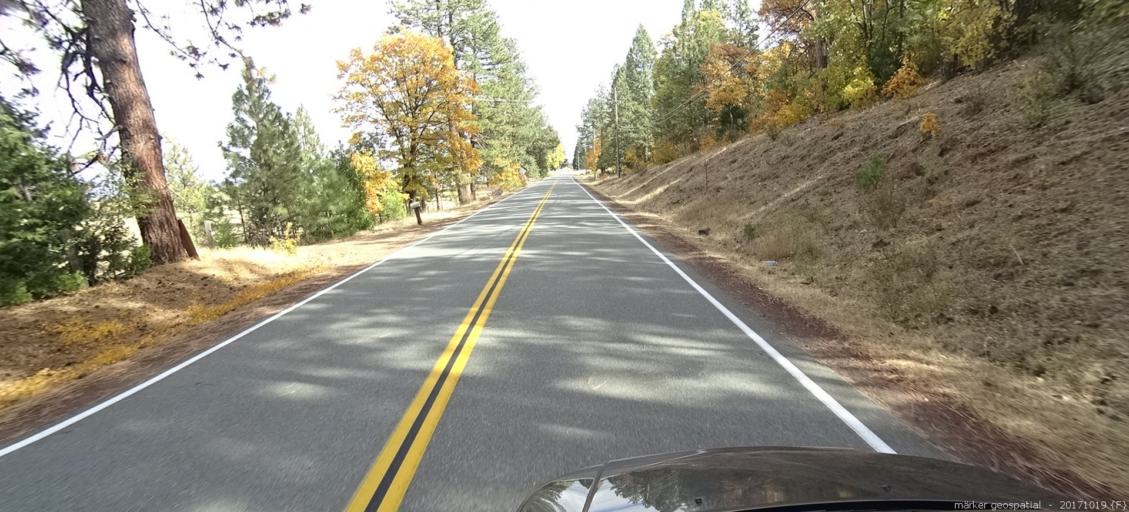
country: US
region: California
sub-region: Shasta County
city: Burney
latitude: 41.0346
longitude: -121.4919
